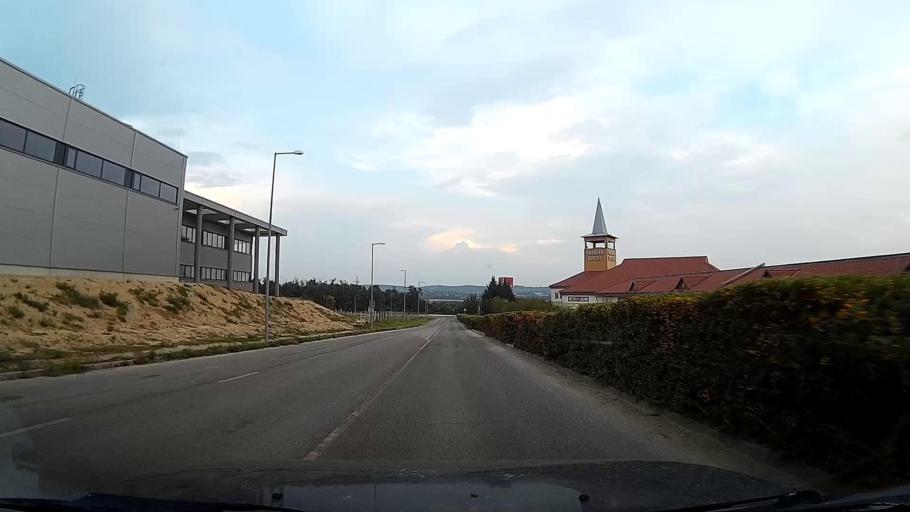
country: HU
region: Pest
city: Toeroekbalint
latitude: 47.4656
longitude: 18.8894
